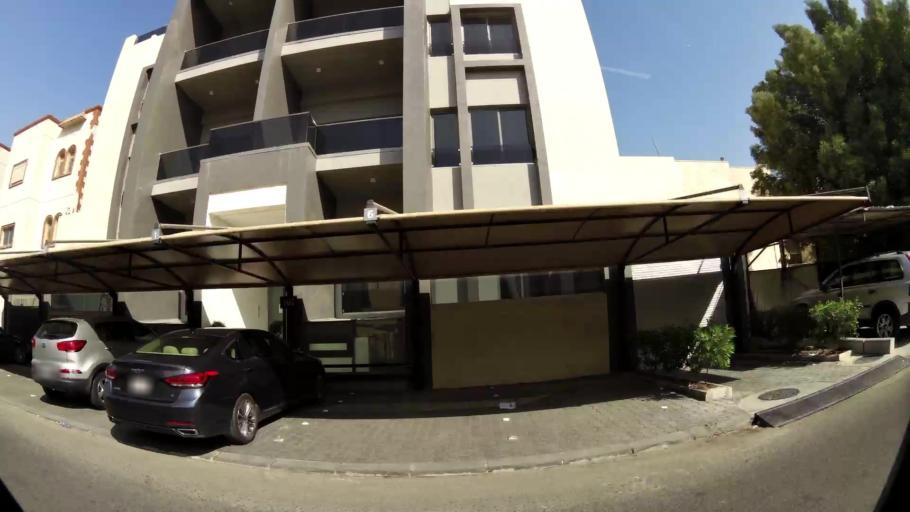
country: KW
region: Muhafazat Hawalli
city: Salwa
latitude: 29.2894
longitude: 48.0849
